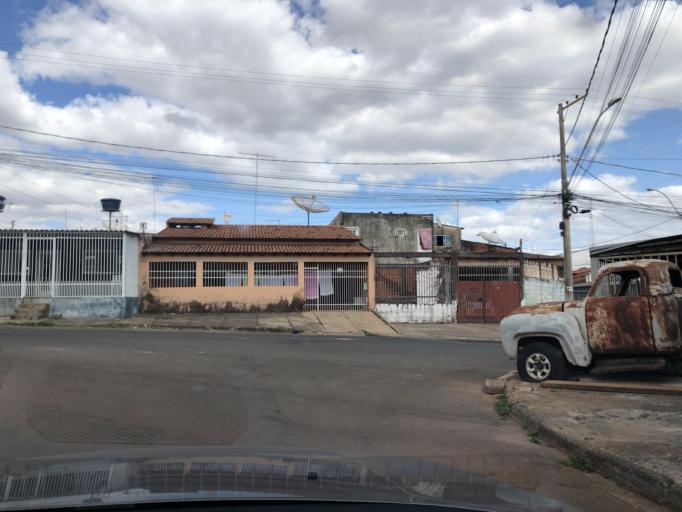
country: BR
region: Federal District
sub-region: Brasilia
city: Brasilia
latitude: -15.8867
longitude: -48.1287
